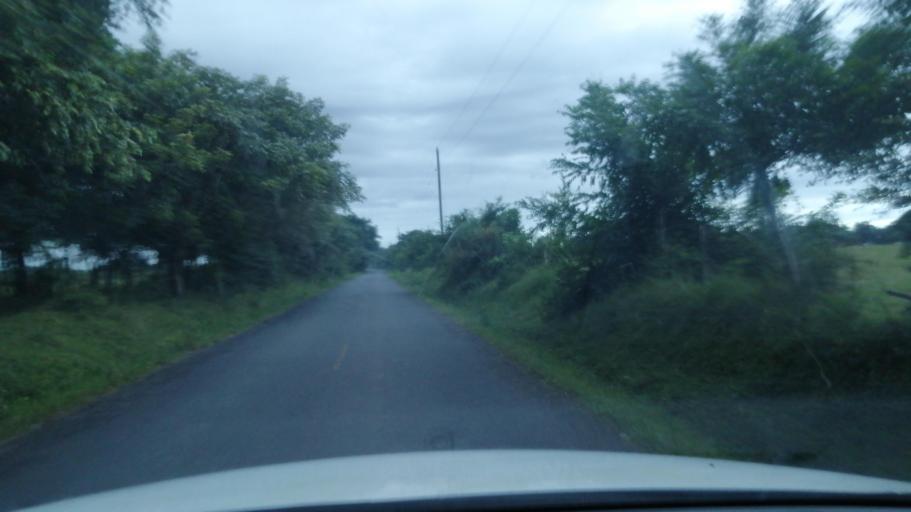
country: PA
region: Chiriqui
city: Alanje
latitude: 8.4081
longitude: -82.5014
